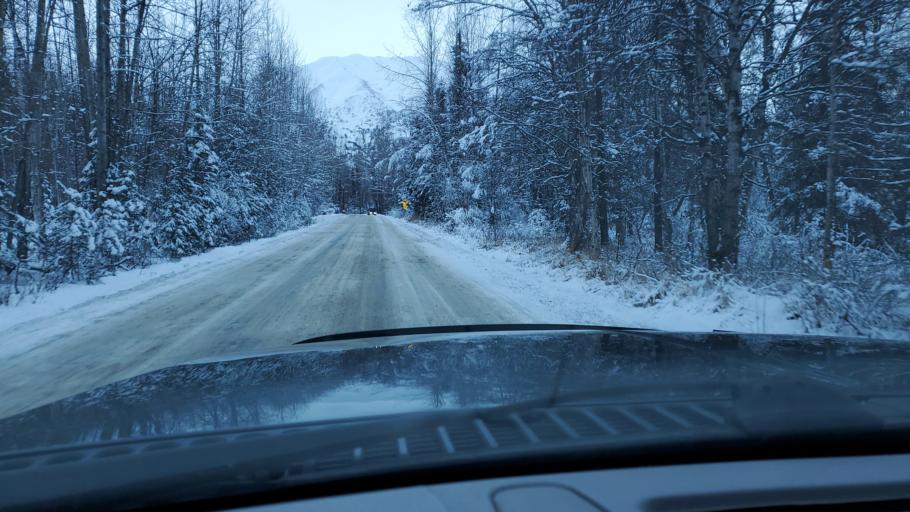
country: US
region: Alaska
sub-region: Matanuska-Susitna Borough
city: Fishhook
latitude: 61.6915
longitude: -149.2998
